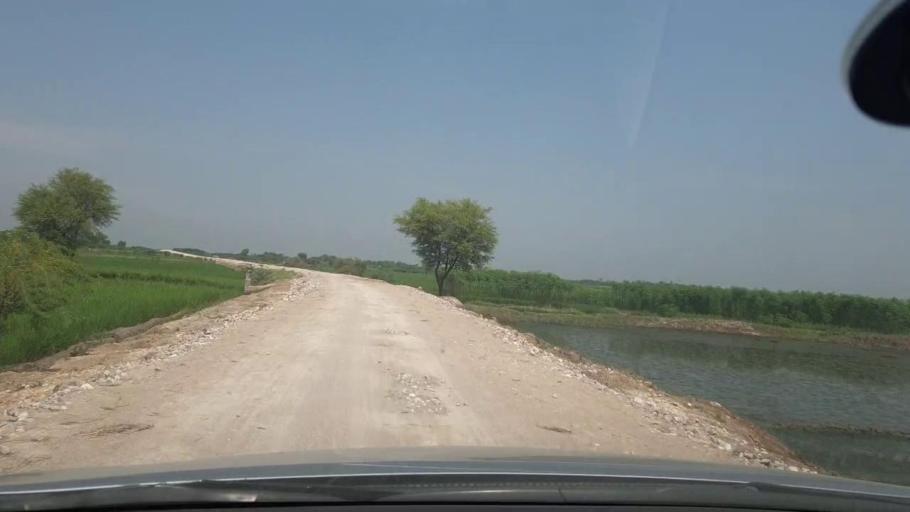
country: PK
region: Balochistan
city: Garhi Khairo
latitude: 28.0575
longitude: 67.9998
